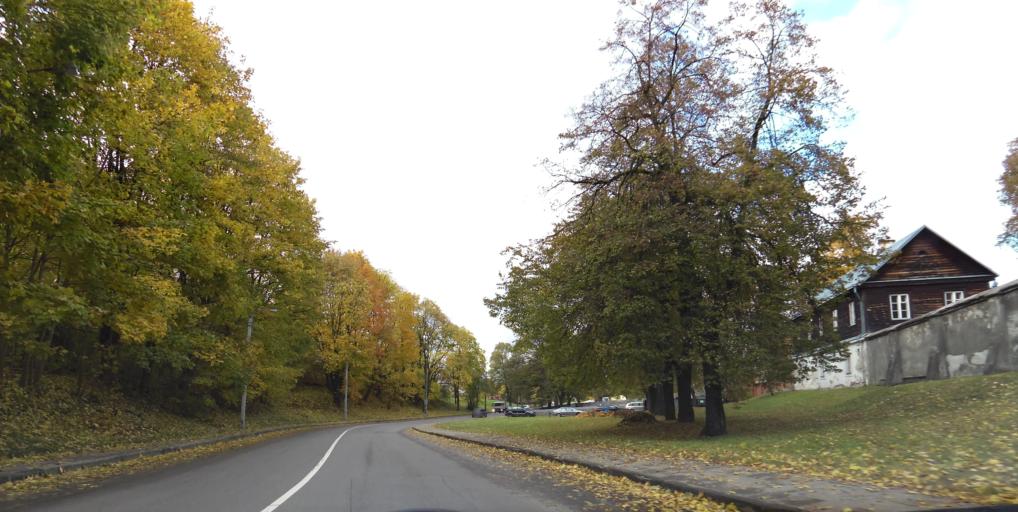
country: LT
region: Vilnius County
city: Rasos
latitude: 54.6695
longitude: 25.3023
